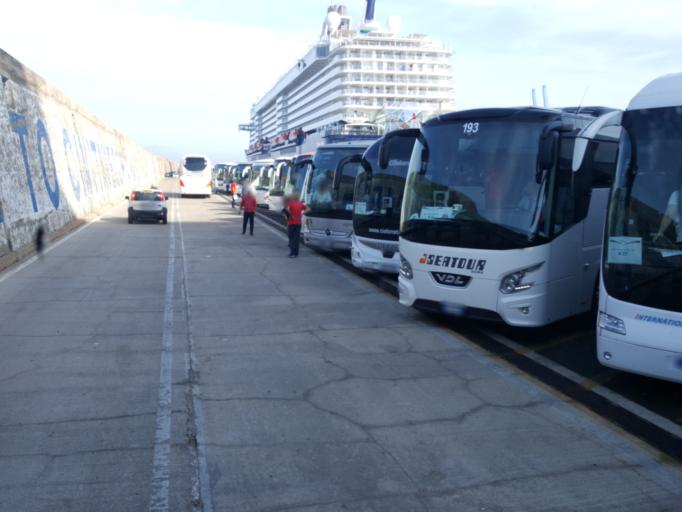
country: IT
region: Latium
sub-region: Citta metropolitana di Roma Capitale
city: Civitavecchia
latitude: 42.0987
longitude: 11.7739
